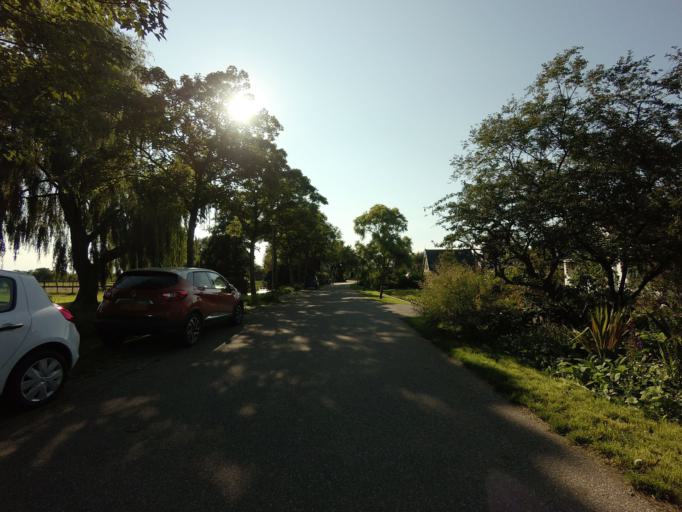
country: NL
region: North Holland
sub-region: Gemeente Enkhuizen
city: Enkhuizen
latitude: 52.6781
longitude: 5.2365
